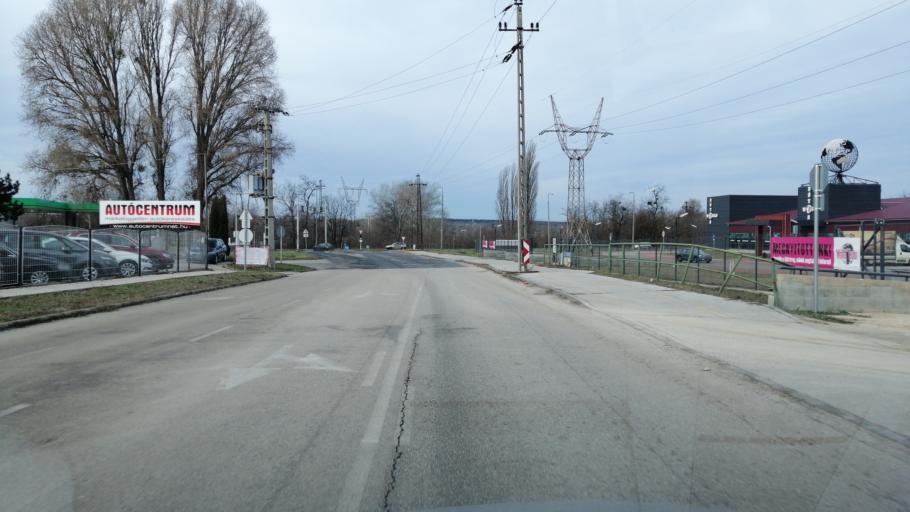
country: HU
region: Komarom-Esztergom
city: Vertesszolos
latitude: 47.6049
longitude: 18.3877
